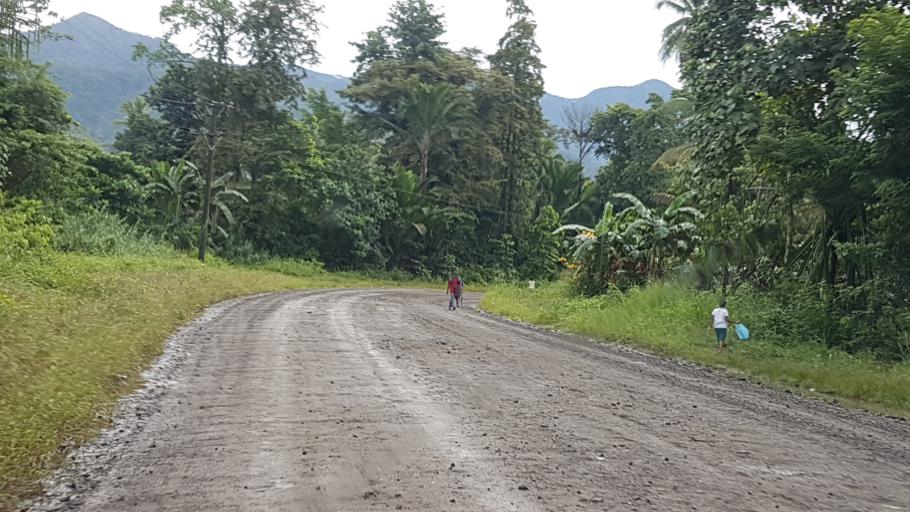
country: PG
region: Milne Bay
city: Alotau
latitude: -10.3211
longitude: 150.4917
